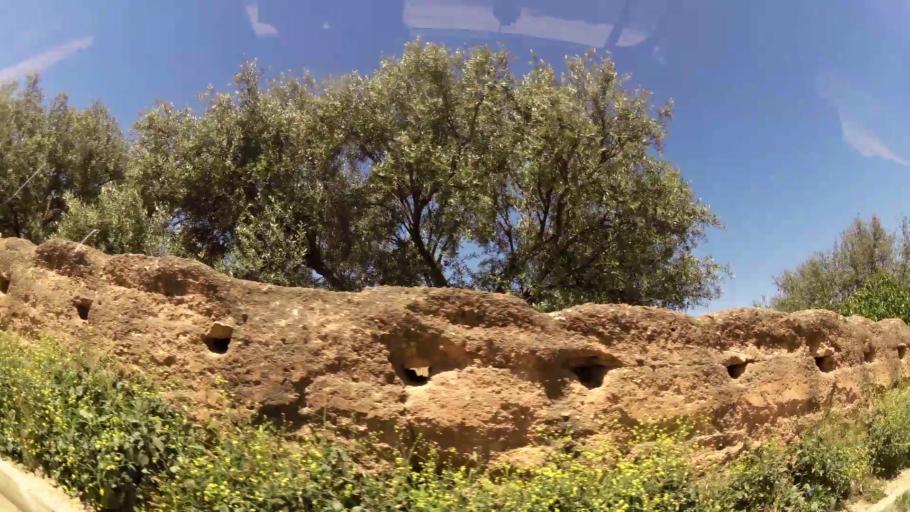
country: MA
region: Meknes-Tafilalet
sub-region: Meknes
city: Meknes
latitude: 33.8556
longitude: -5.5545
